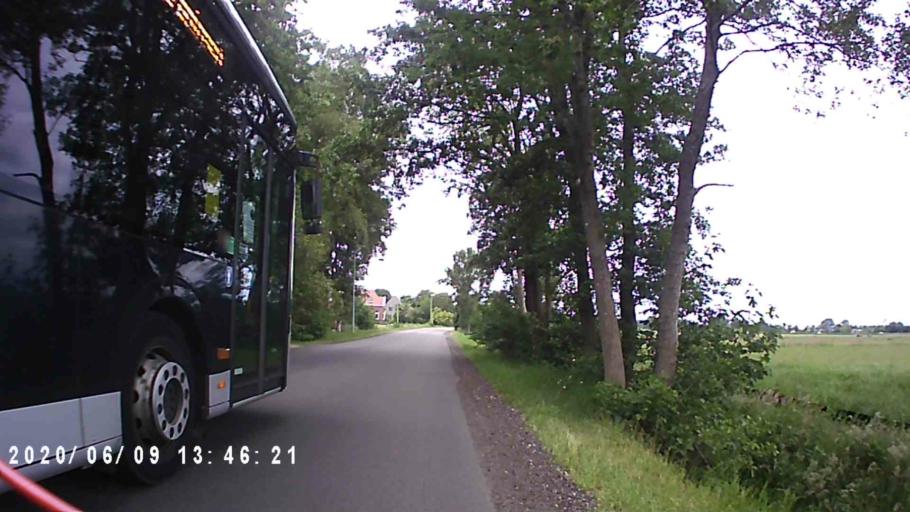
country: NL
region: Groningen
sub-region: Gemeente Groningen
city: Oosterpark
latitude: 53.2234
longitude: 6.6356
